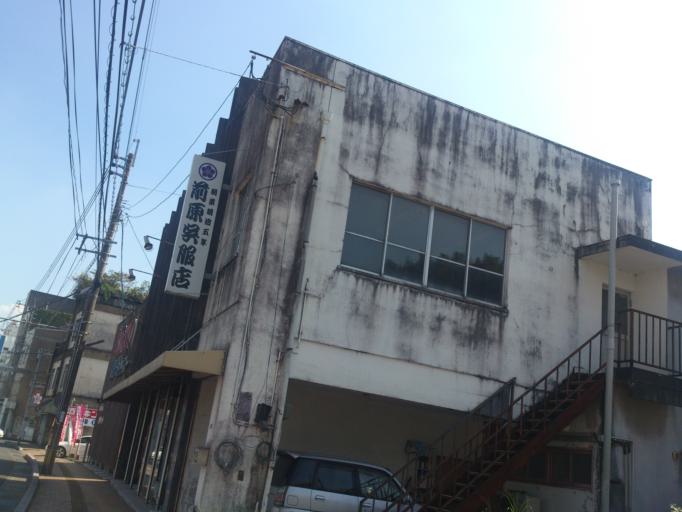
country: JP
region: Kagoshima
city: Kanoya
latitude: 31.3861
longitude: 130.8502
